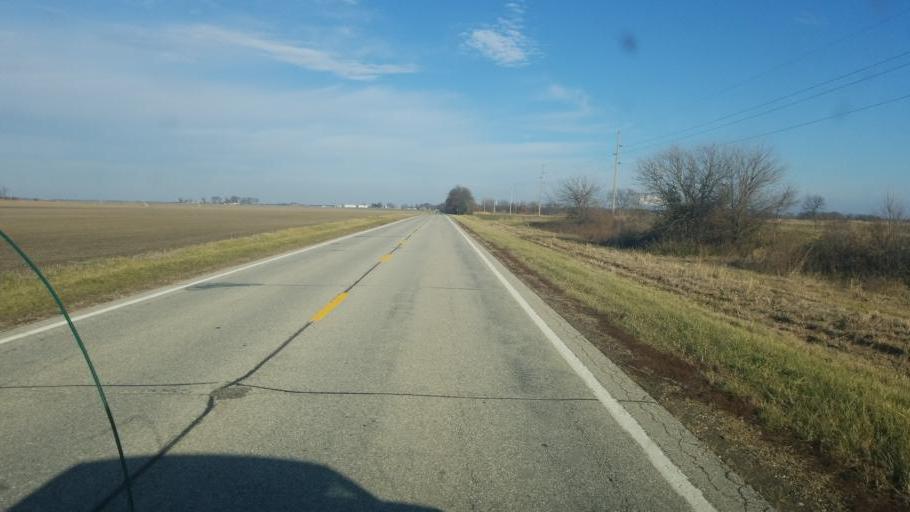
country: US
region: Illinois
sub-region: Edwards County
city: Grayville
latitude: 38.3360
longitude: -87.8951
